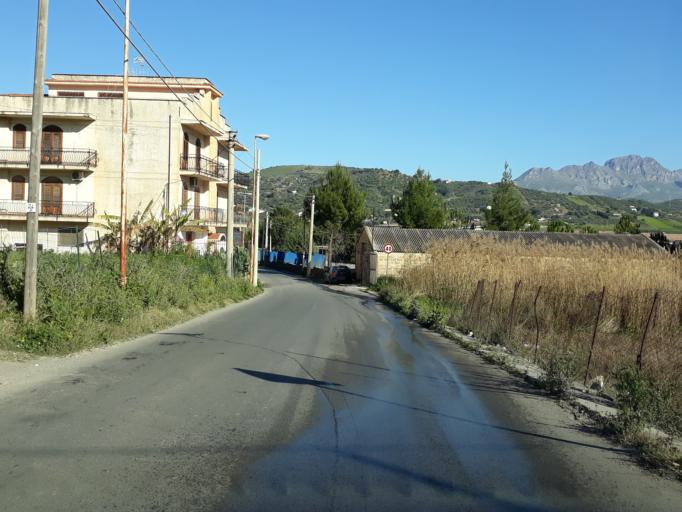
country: IT
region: Sicily
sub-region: Palermo
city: Misilmeri
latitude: 38.0277
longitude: 13.4533
